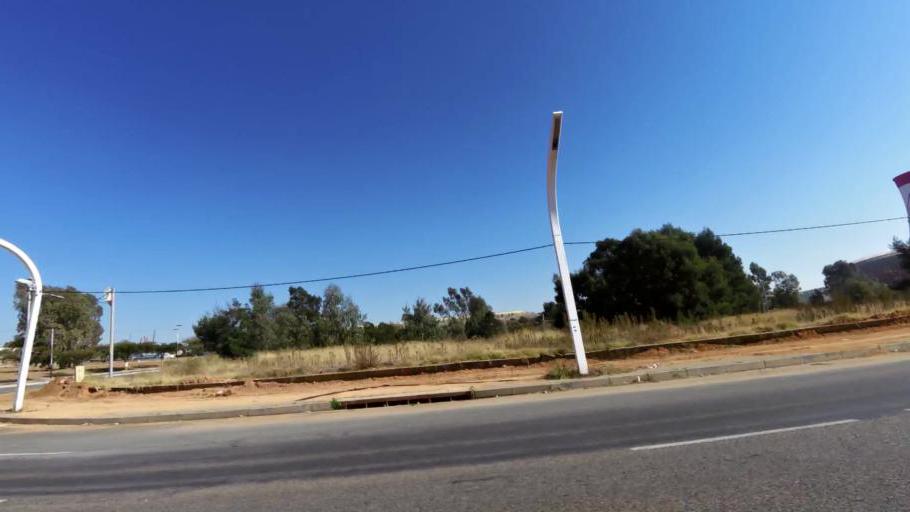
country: ZA
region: Gauteng
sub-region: City of Johannesburg Metropolitan Municipality
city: Johannesburg
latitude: -26.2388
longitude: 27.9855
